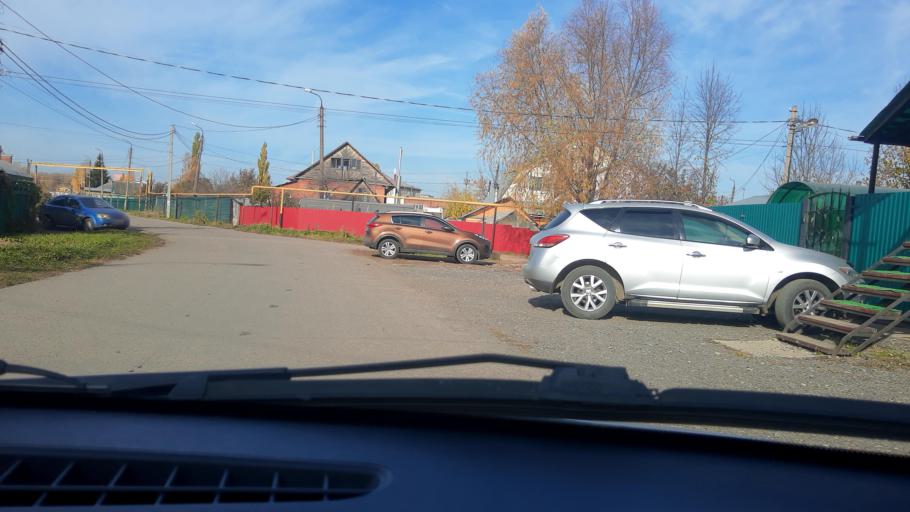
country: RU
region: Bashkortostan
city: Ufa
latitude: 54.7808
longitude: 56.0609
